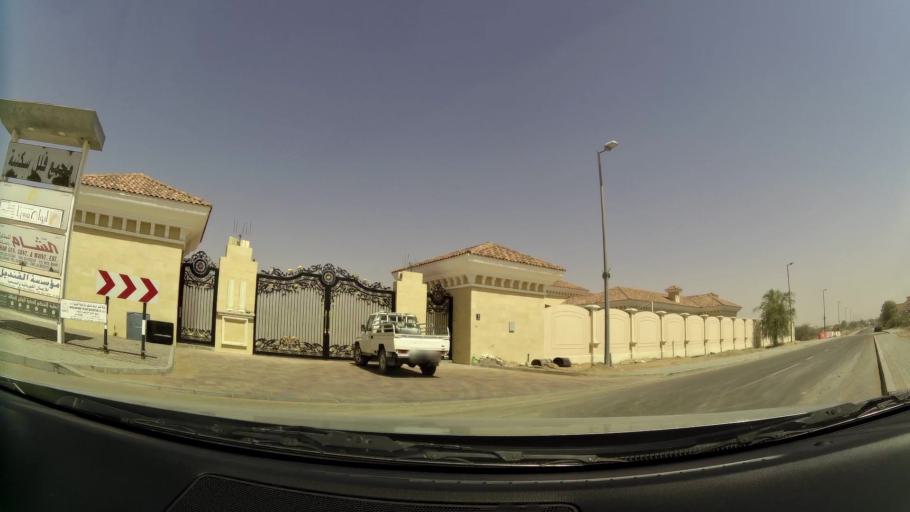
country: OM
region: Al Buraimi
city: Al Buraymi
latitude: 24.2881
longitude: 55.7582
